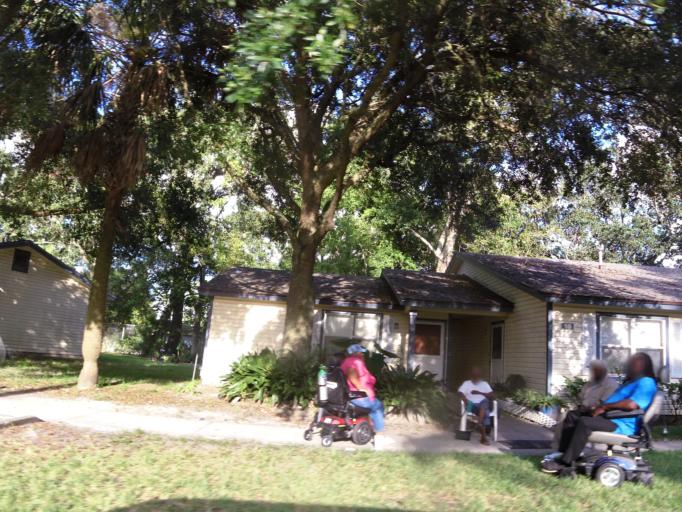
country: US
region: Florida
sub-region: Duval County
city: Jacksonville
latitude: 30.3428
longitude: -81.6657
